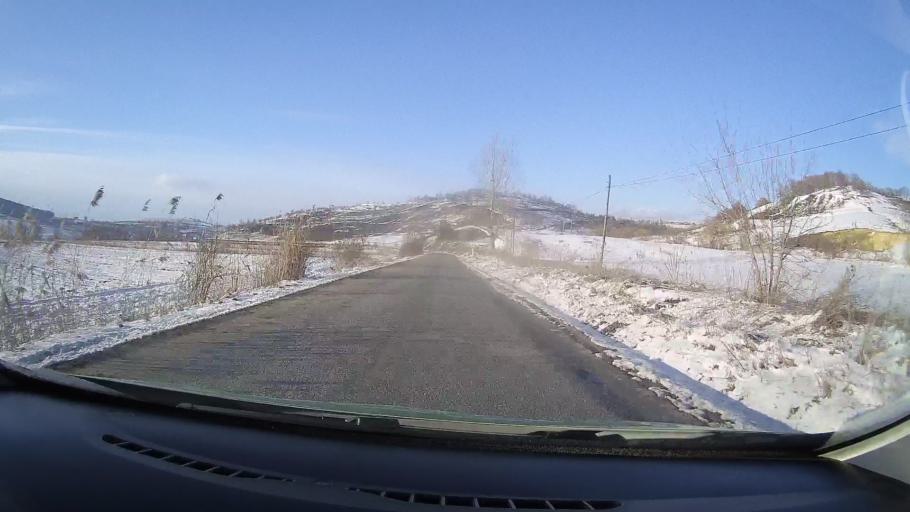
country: RO
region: Sibiu
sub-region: Comuna Merghindeal
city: Merghindeal
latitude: 45.9730
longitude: 24.7072
